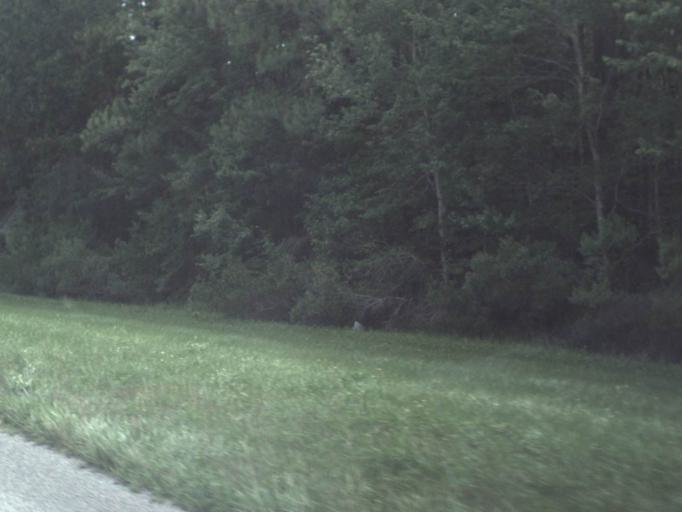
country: US
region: Florida
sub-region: Duval County
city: Baldwin
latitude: 30.2208
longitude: -82.0074
